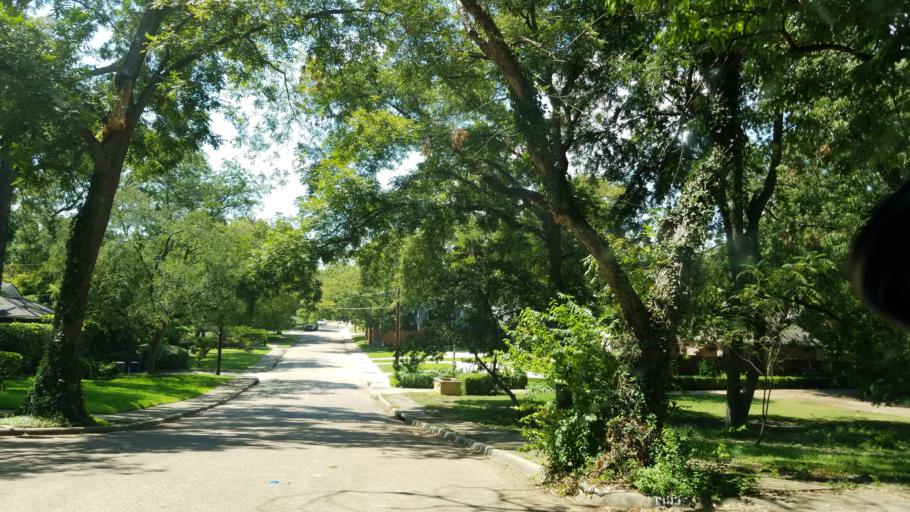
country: US
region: Texas
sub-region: Dallas County
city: Richardson
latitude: 32.8830
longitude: -96.7115
